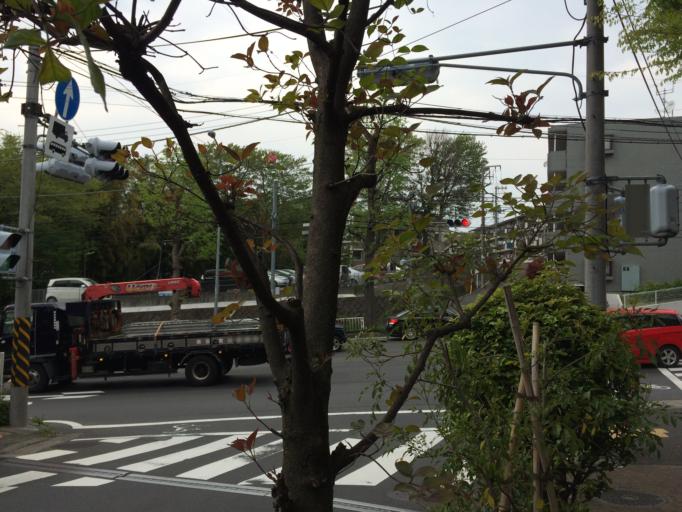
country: JP
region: Kanagawa
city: Yokohama
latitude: 35.5188
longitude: 139.6352
